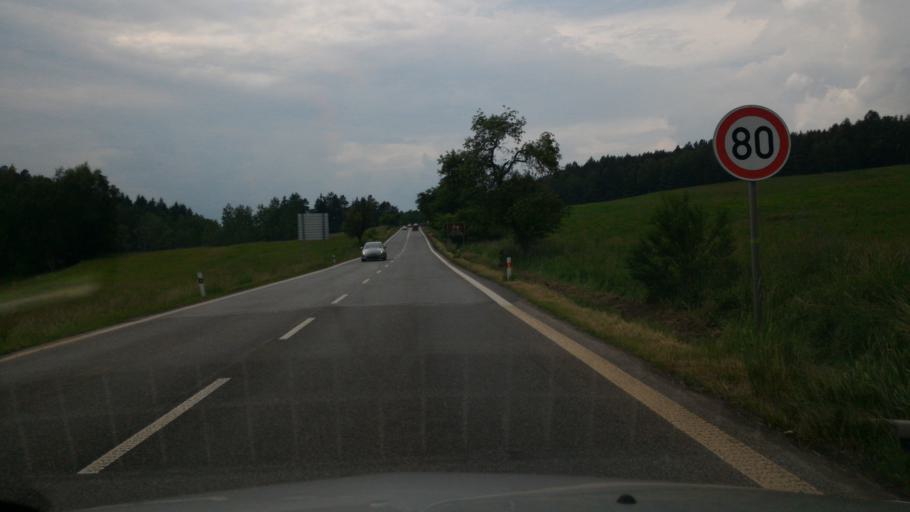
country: CZ
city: Jablonne v Podjestedi
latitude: 50.7867
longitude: 14.8039
